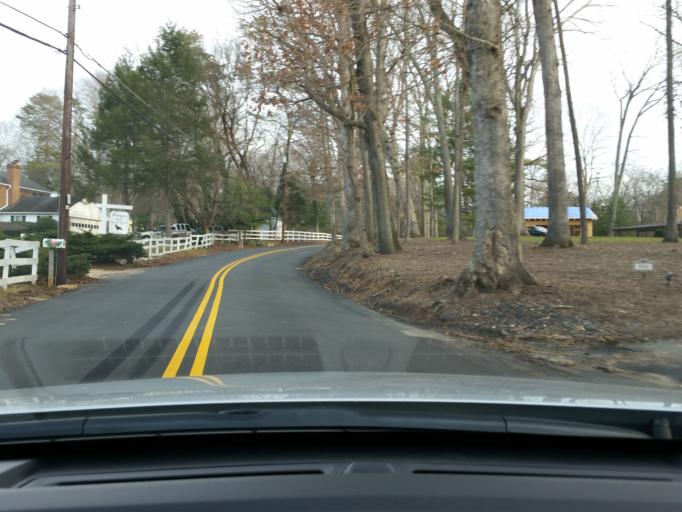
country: US
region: Virginia
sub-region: Fairfax County
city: Great Falls
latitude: 38.9833
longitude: -77.2742
